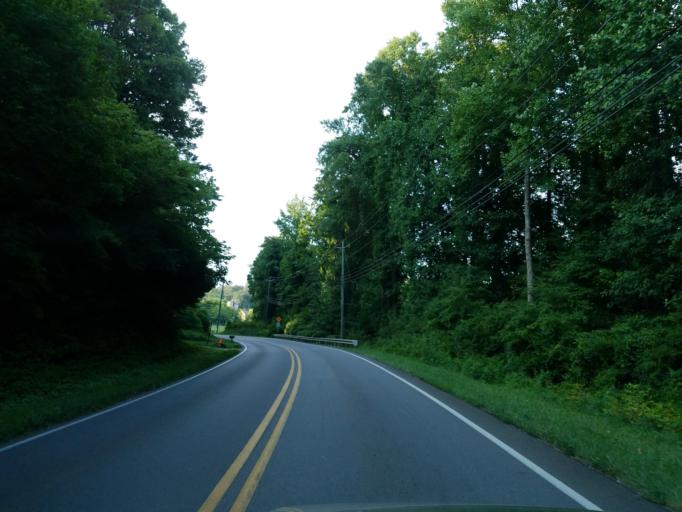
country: US
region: Georgia
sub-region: Gilmer County
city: Ellijay
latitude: 34.6537
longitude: -84.4998
